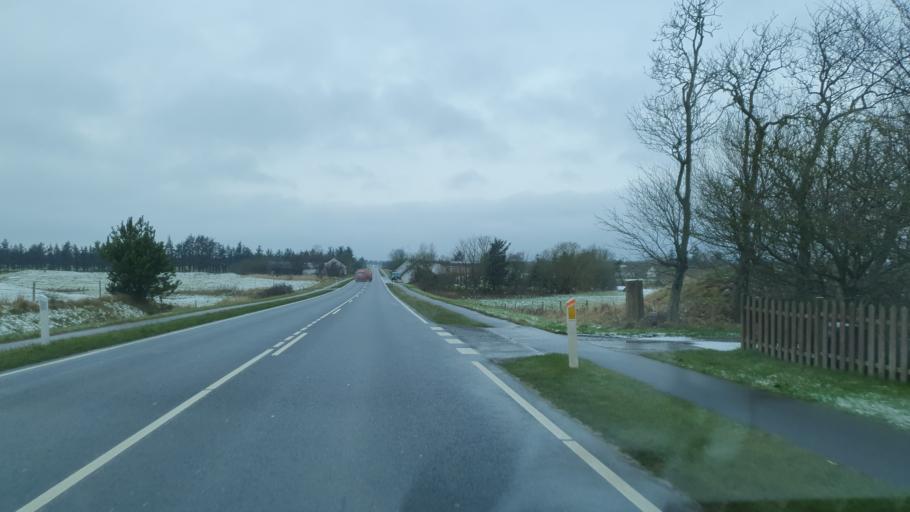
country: DK
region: North Denmark
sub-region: Jammerbugt Kommune
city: Fjerritslev
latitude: 57.0887
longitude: 9.2400
